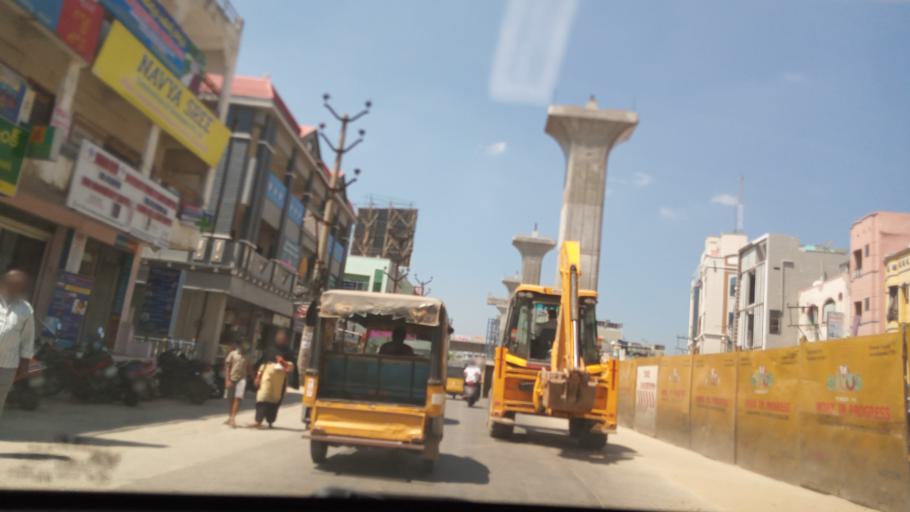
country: IN
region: Andhra Pradesh
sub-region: Chittoor
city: Tirupati
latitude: 13.6422
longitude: 79.4296
